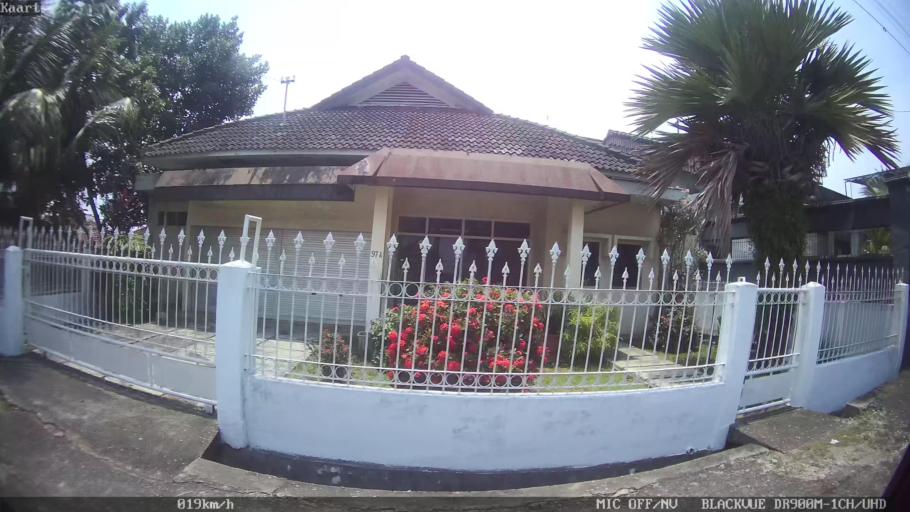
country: ID
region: Lampung
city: Bandarlampung
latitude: -5.4244
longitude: 105.2627
